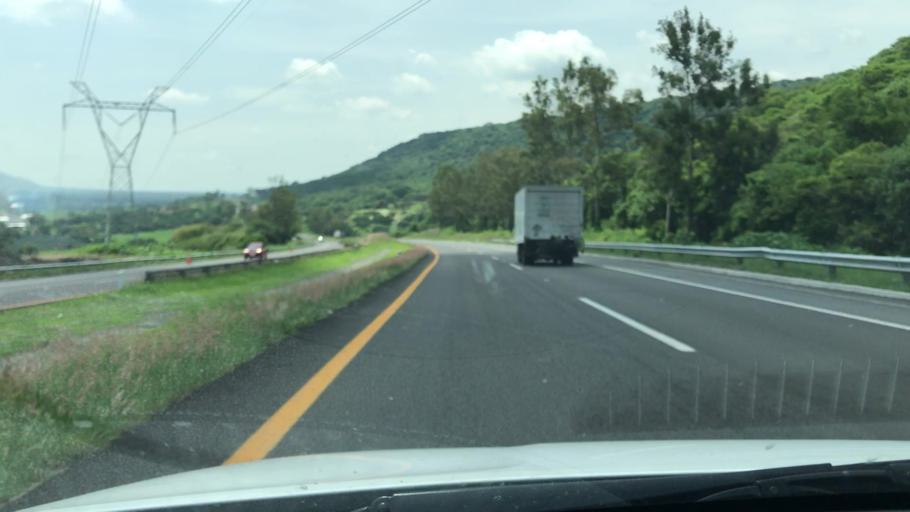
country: MX
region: Jalisco
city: Ocotlan
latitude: 20.4228
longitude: -102.7684
